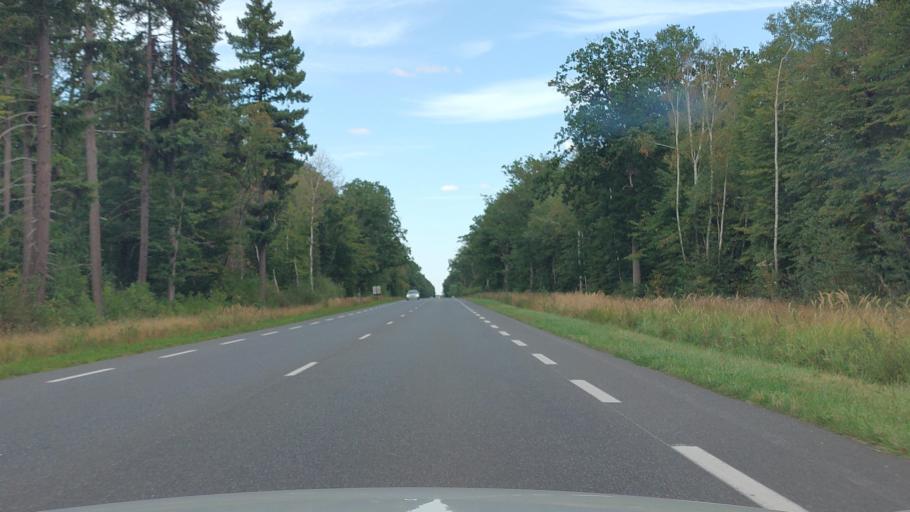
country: FR
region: Ile-de-France
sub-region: Departement de Seine-et-Marne
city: La Chapelle-Gauthier
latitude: 48.5449
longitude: 2.8421
